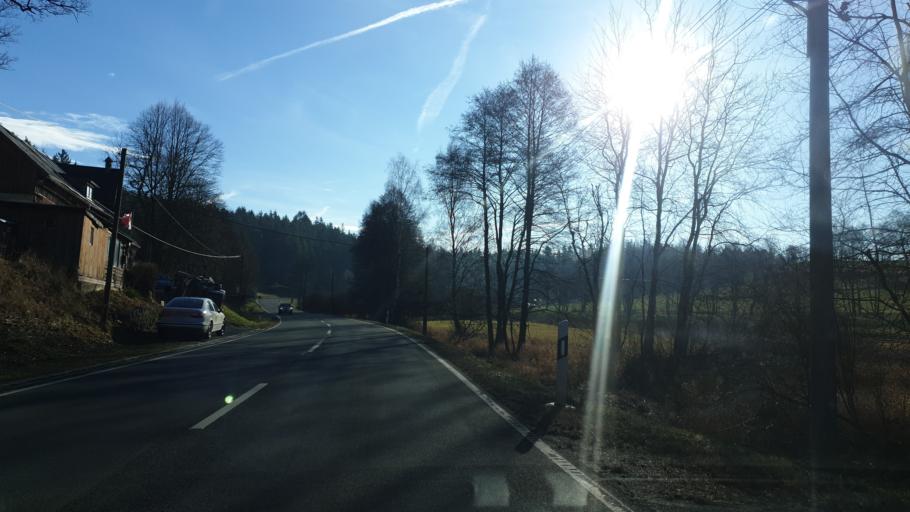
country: DE
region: Saxony
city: Bad Brambach
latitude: 50.2589
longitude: 12.3010
